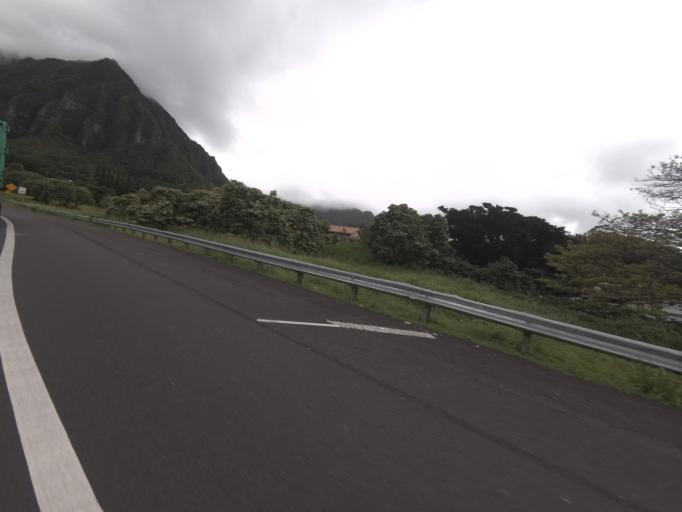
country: US
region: Hawaii
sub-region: Honolulu County
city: Kane'ohe
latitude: 21.4030
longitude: -157.8074
